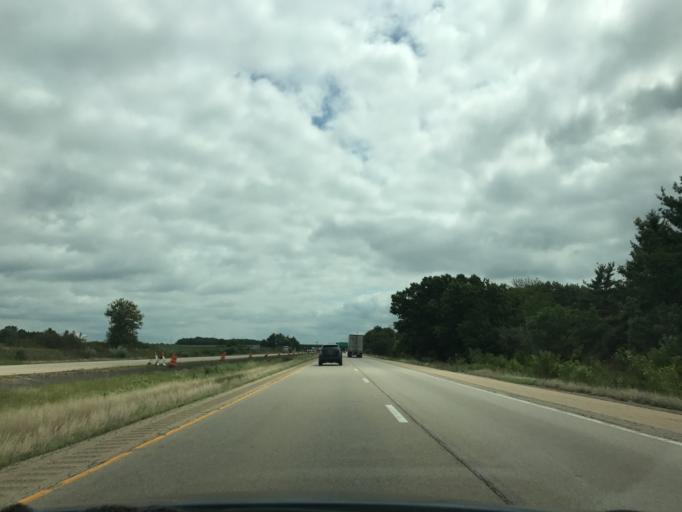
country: US
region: Illinois
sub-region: LaSalle County
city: La Salle
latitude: 41.3709
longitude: -89.0750
